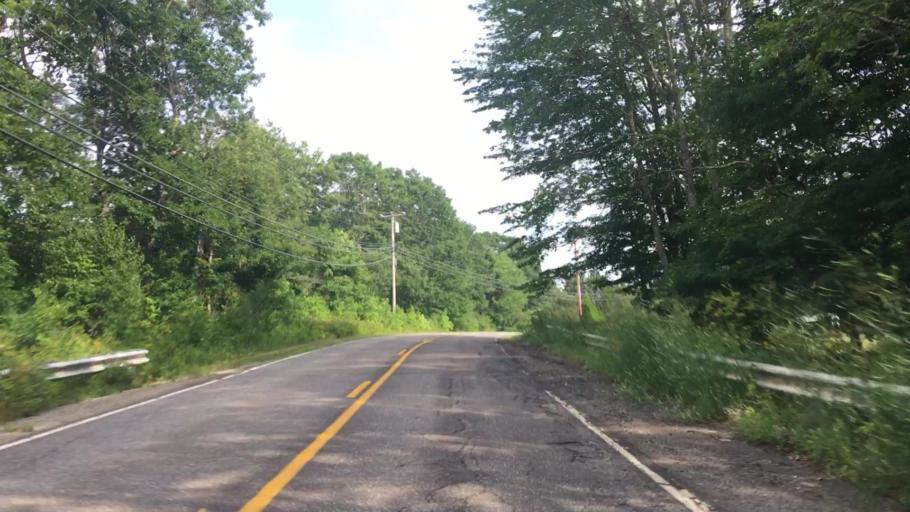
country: US
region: Maine
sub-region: Lincoln County
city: Waldoboro
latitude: 44.0655
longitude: -69.3479
